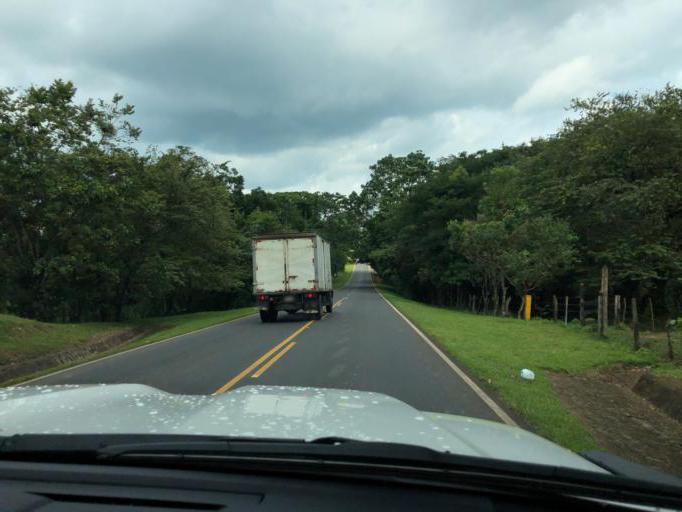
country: NI
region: Chontales
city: Villa Sandino
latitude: 11.9976
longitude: -84.8431
